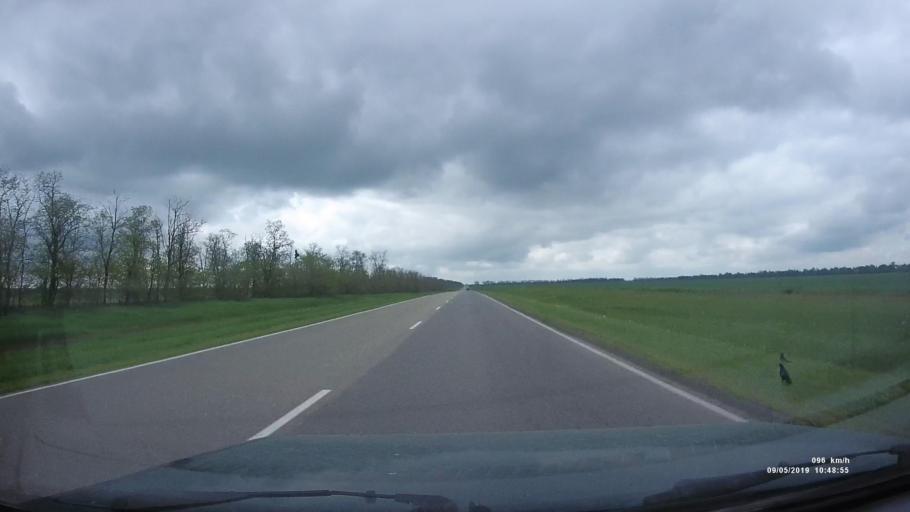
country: RU
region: Rostov
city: Peshkovo
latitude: 46.9498
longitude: 39.3555
